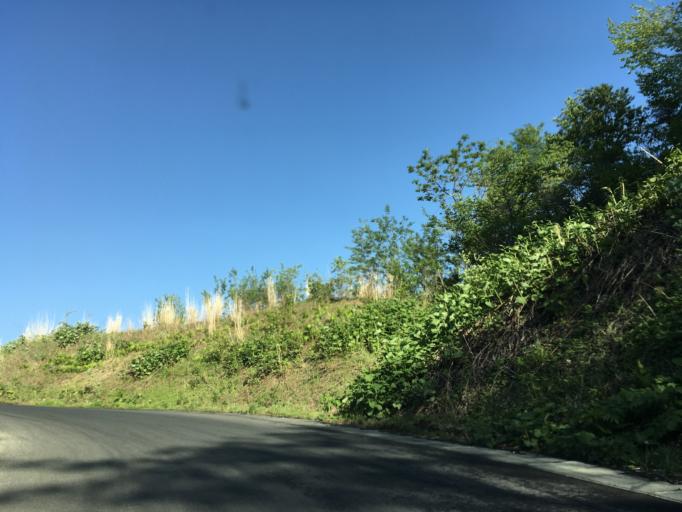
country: JP
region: Iwate
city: Mizusawa
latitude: 39.1219
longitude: 140.9266
